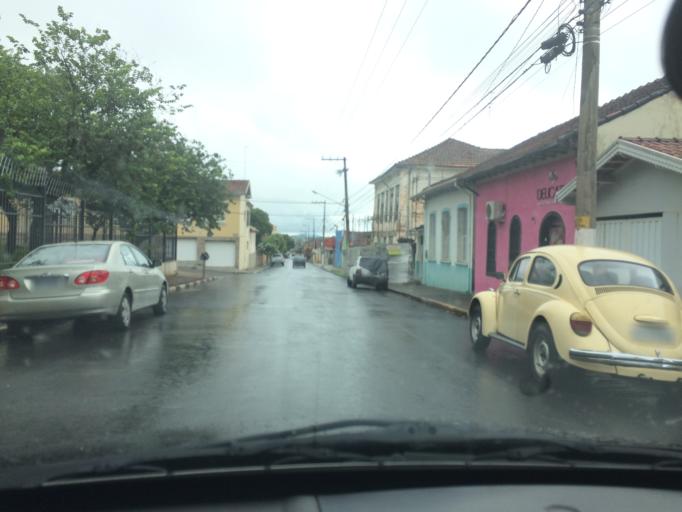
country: BR
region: Sao Paulo
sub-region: Casa Branca
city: Casa Branca
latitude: -21.7737
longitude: -47.0822
